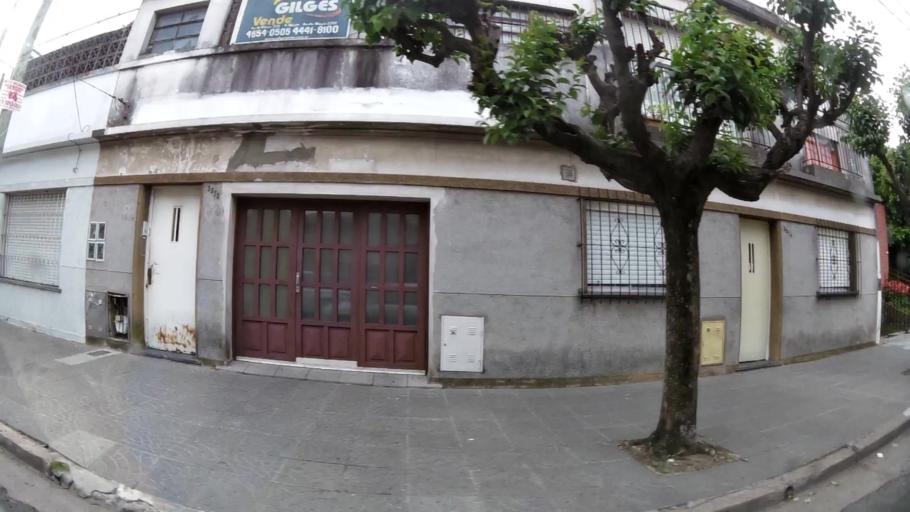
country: AR
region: Buenos Aires
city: San Justo
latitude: -34.6684
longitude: -58.5255
